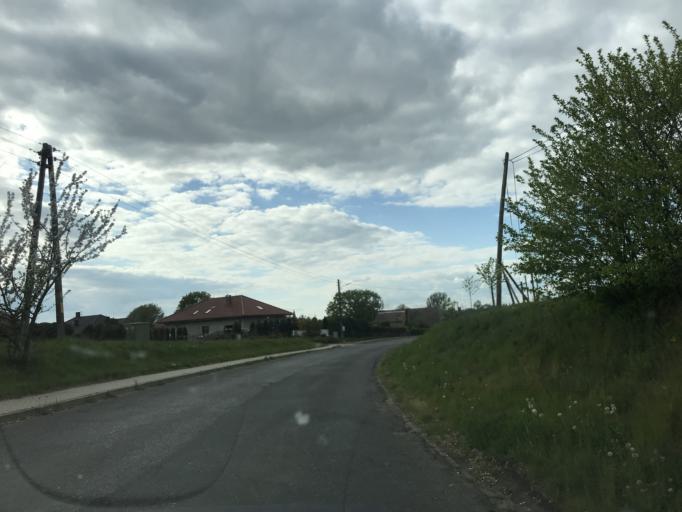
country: PL
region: West Pomeranian Voivodeship
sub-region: Powiat mysliborski
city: Mysliborz
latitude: 52.9170
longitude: 14.8873
